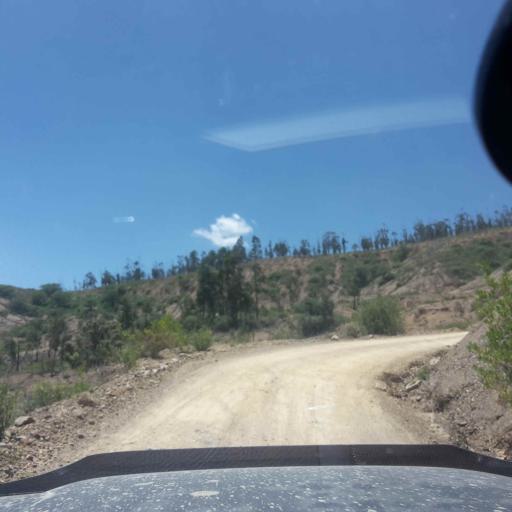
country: BO
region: Cochabamba
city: Totora
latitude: -17.7674
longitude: -65.2398
